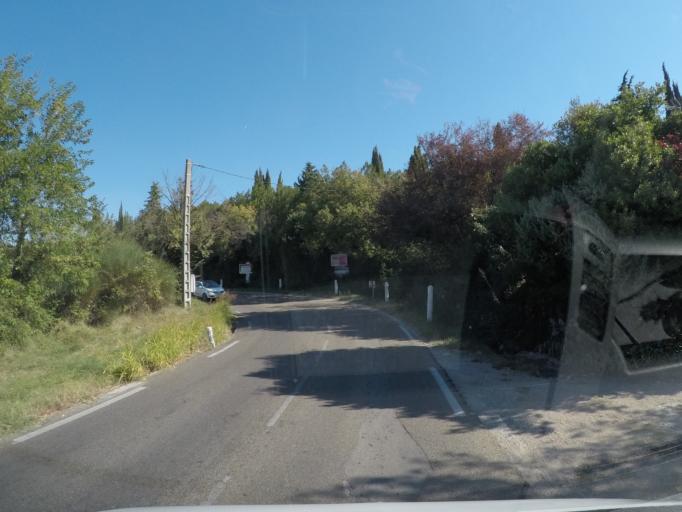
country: FR
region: Languedoc-Roussillon
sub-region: Departement du Gard
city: Uzes
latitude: 44.0049
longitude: 4.4040
